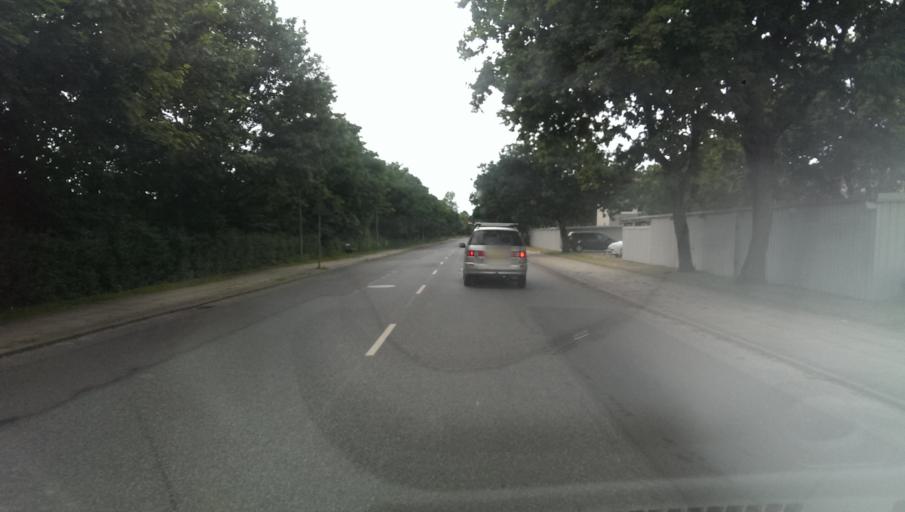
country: DK
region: South Denmark
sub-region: Esbjerg Kommune
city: Esbjerg
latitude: 55.4766
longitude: 8.4995
